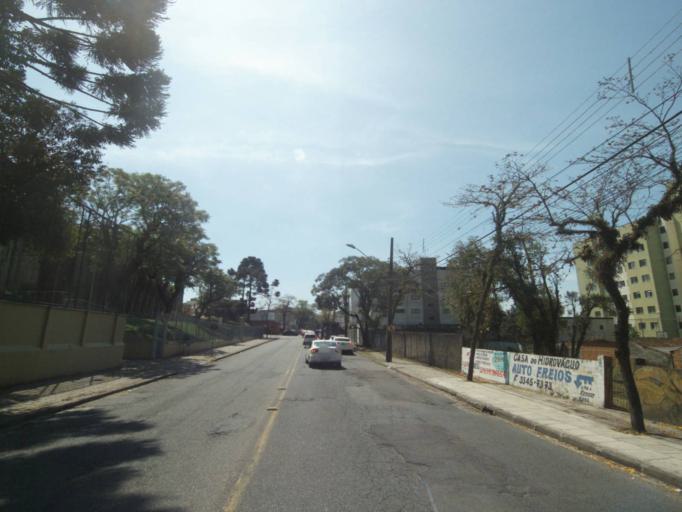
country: BR
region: Parana
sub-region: Curitiba
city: Curitiba
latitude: -25.4755
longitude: -49.2878
